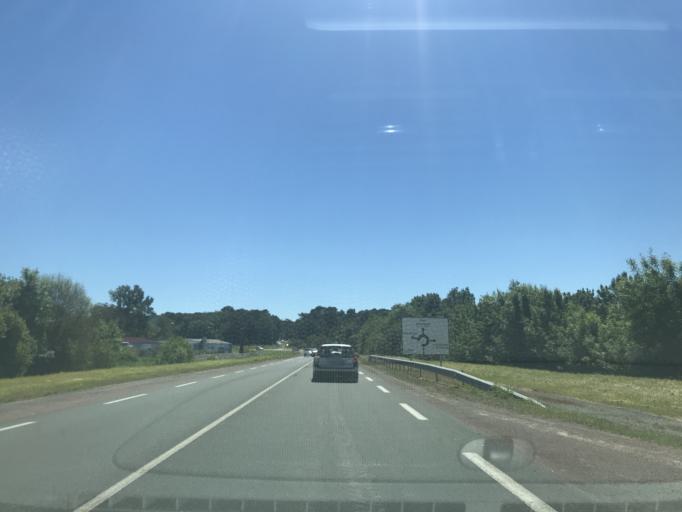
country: FR
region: Poitou-Charentes
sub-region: Departement de la Charente-Maritime
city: Saint-Georges-de-Didonne
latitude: 45.5990
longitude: -0.9742
